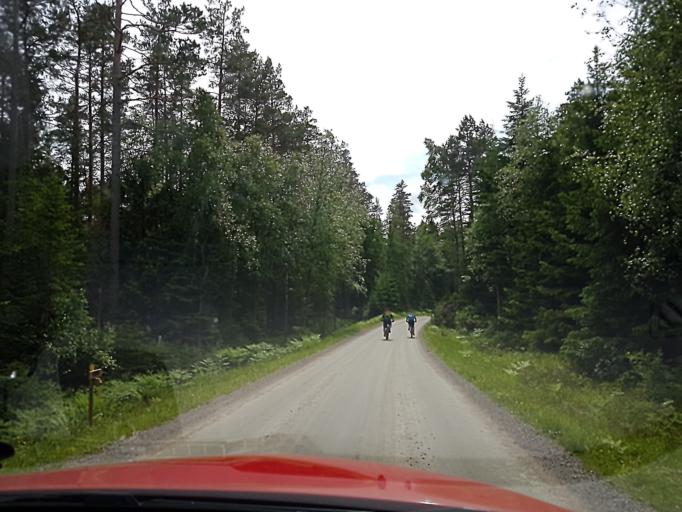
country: SE
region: Vaestra Goetaland
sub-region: Karlsborgs Kommun
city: Karlsborg
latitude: 58.7298
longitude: 14.5914
